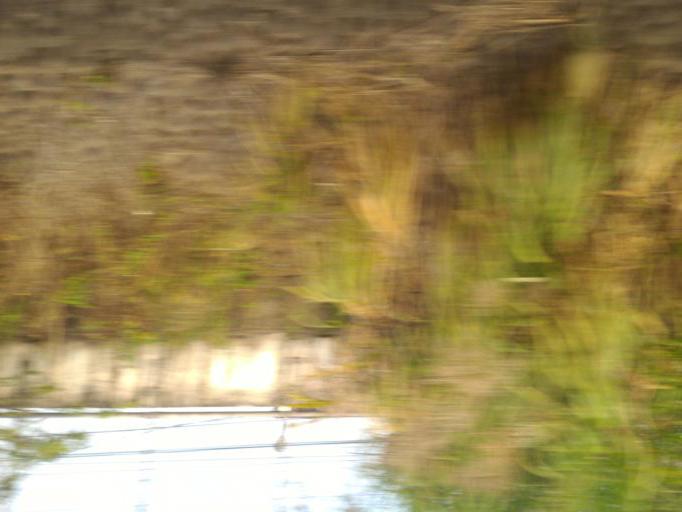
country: TW
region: Taiwan
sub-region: Taoyuan
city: Taoyuan
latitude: 24.9746
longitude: 121.3349
